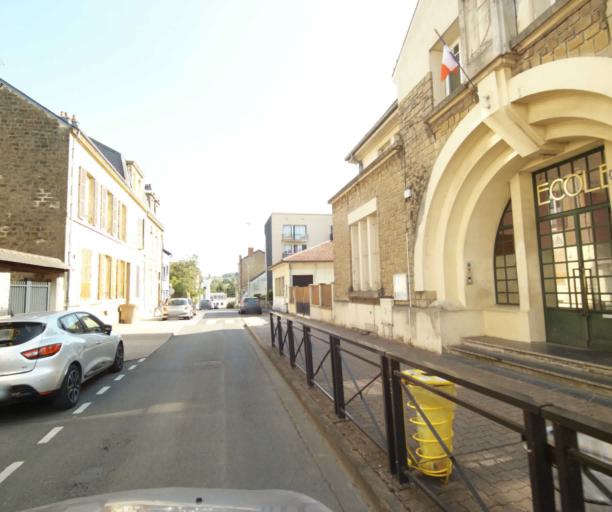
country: FR
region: Champagne-Ardenne
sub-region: Departement des Ardennes
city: Charleville-Mezieres
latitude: 49.7763
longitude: 4.7131
